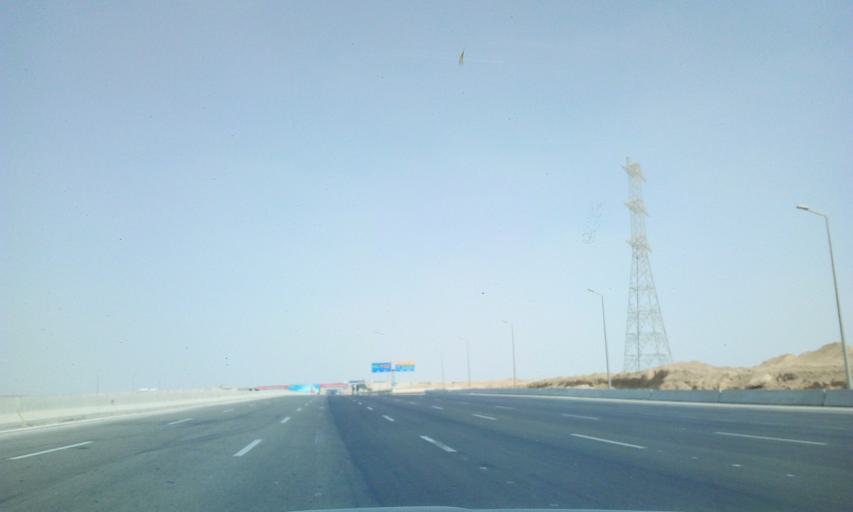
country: EG
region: Muhafazat al Qahirah
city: Halwan
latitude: 29.9062
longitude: 31.6867
